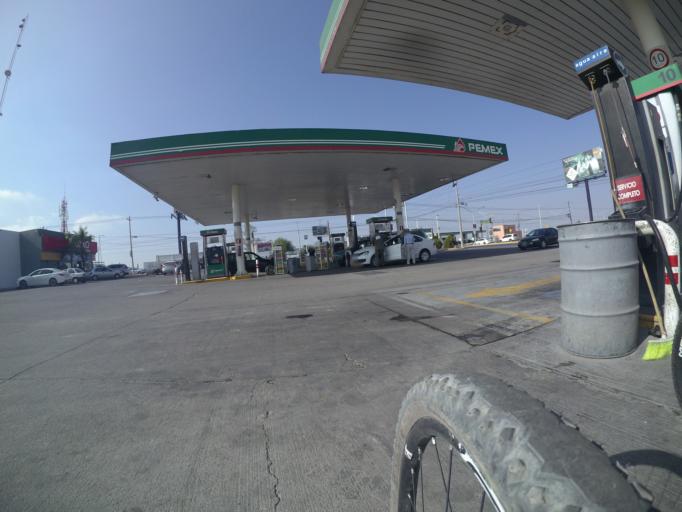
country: MX
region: Aguascalientes
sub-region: Jesus Maria
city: Arboledas Paso Blanco [Fraccionamiento]
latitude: 21.9465
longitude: -102.2968
